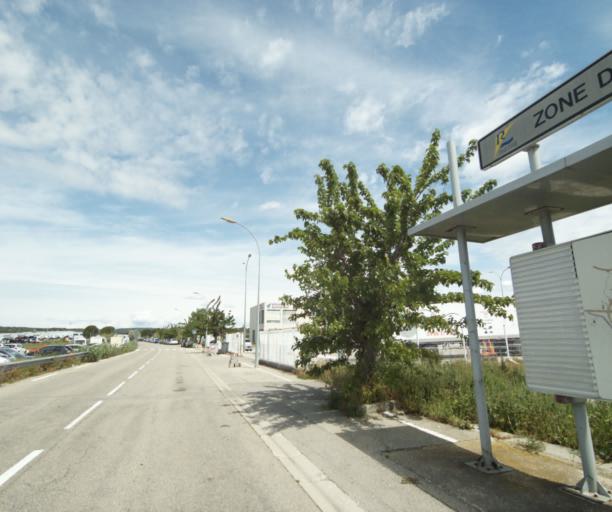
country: FR
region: Provence-Alpes-Cote d'Azur
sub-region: Departement des Bouches-du-Rhone
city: Rognac
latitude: 43.4945
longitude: 5.2262
